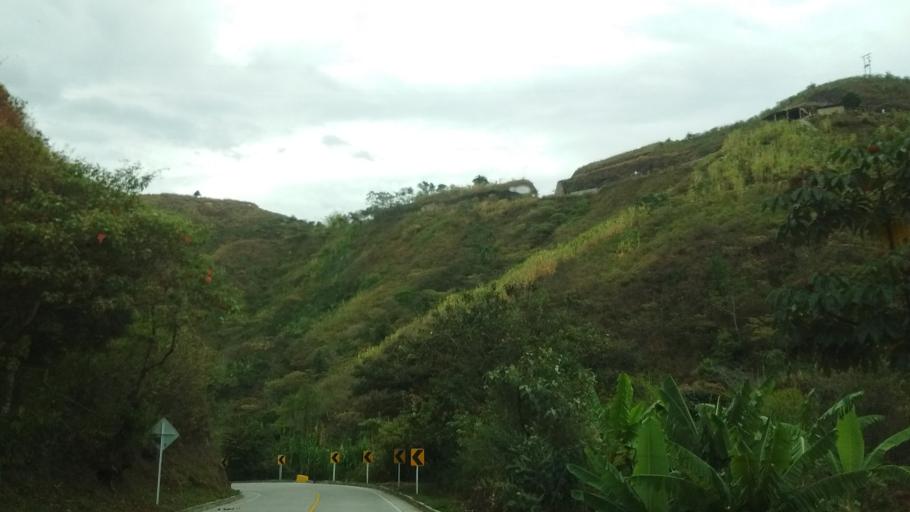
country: CO
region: Cauca
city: La Sierra
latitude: 2.1581
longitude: -76.7683
